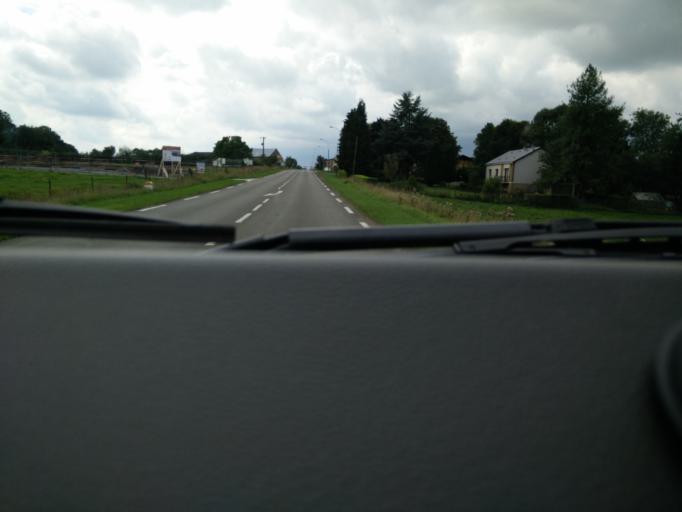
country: FR
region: Champagne-Ardenne
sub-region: Departement des Ardennes
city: Signy-le-Petit
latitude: 49.8729
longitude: 4.3705
